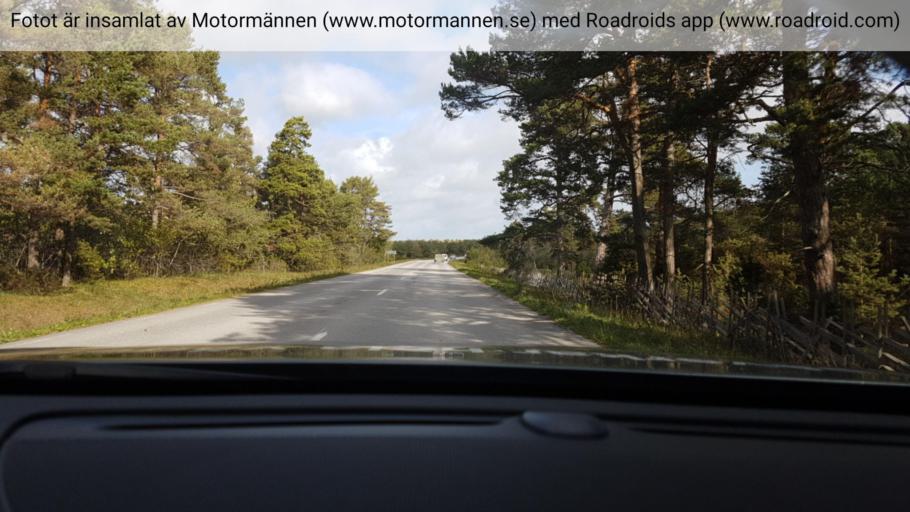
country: SE
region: Gotland
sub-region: Gotland
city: Slite
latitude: 57.8867
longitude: 19.0894
